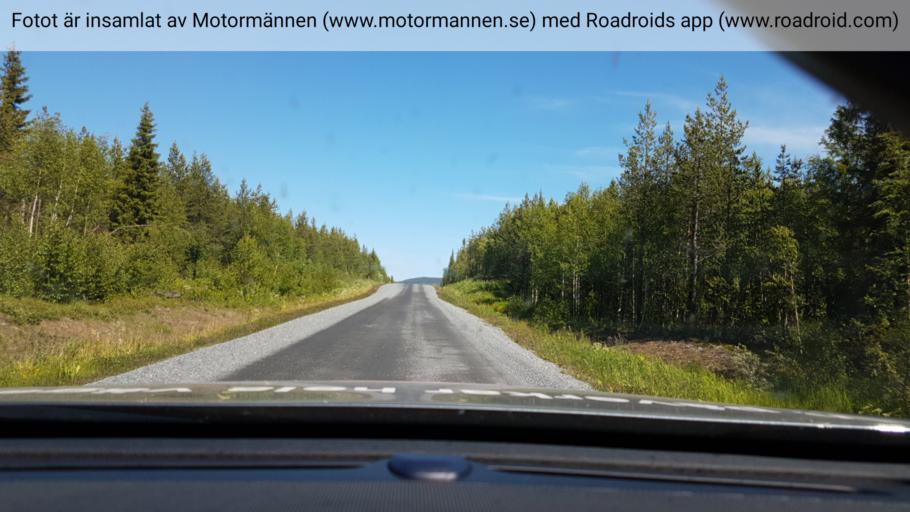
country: SE
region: Vaesterbotten
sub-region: Vilhelmina Kommun
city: Sjoberg
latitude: 64.7941
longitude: 15.9862
